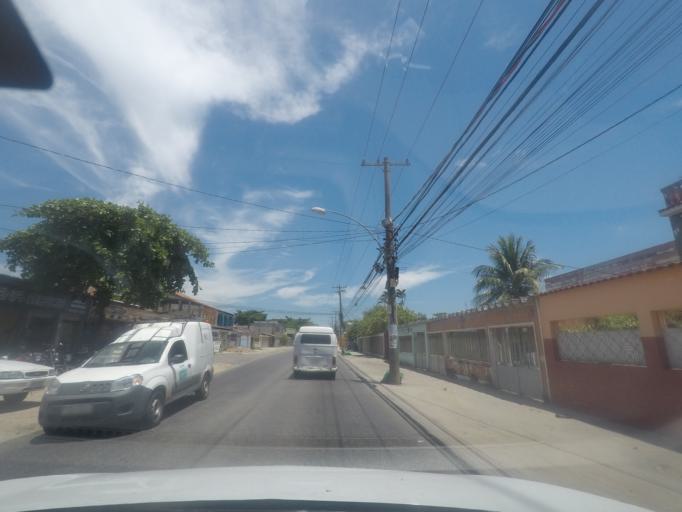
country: BR
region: Rio de Janeiro
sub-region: Itaguai
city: Itaguai
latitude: -22.9442
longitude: -43.6826
